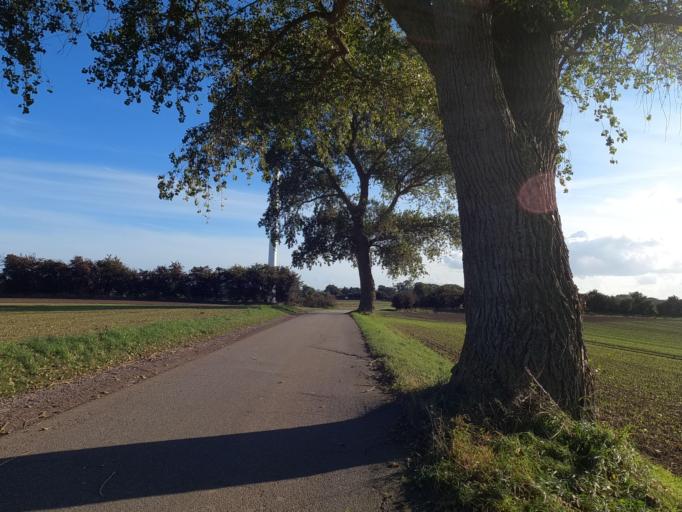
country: DE
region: Schleswig-Holstein
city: Neukirchen
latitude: 54.3404
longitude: 11.0508
